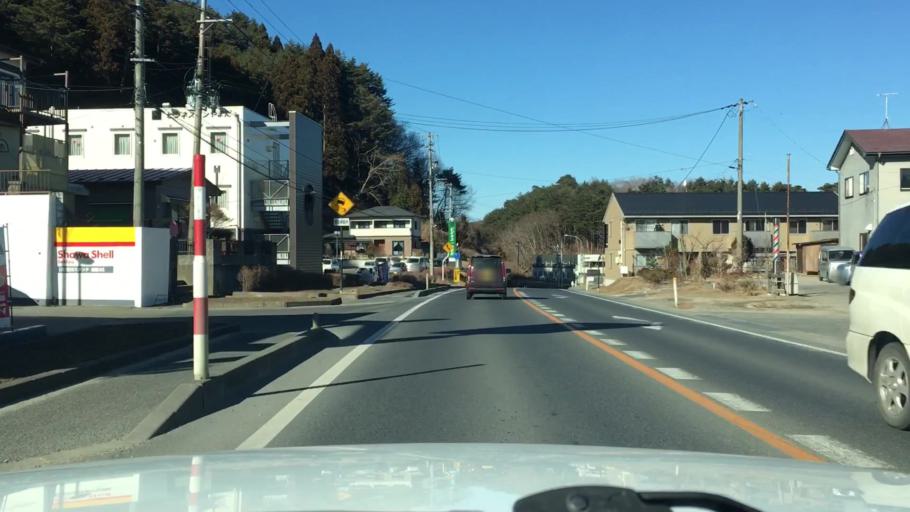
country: JP
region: Iwate
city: Yamada
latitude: 39.4441
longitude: 141.9706
